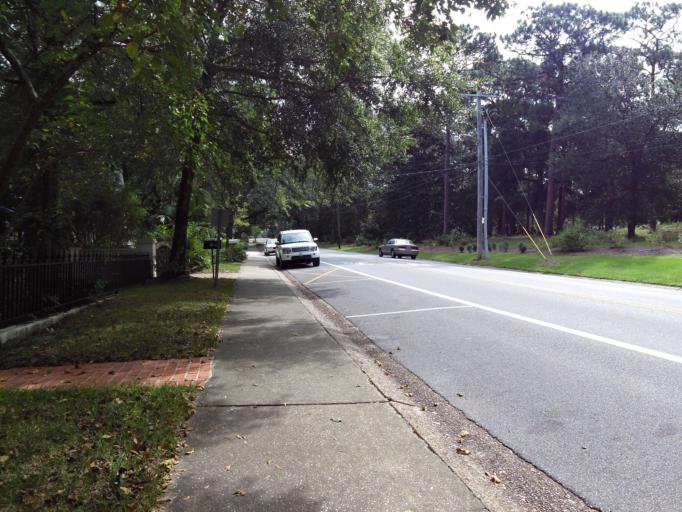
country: US
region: Alabama
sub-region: Baldwin County
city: Fairhope
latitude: 30.5245
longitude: -87.9096
